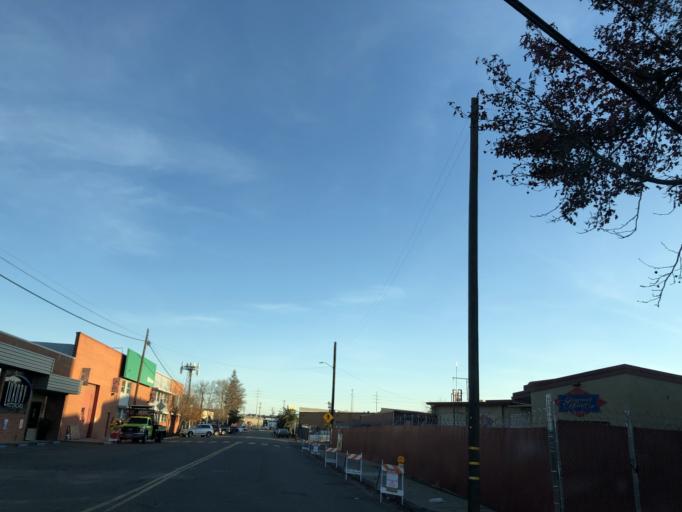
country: US
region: California
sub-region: Sacramento County
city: Rosemont
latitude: 38.5557
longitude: -121.4264
